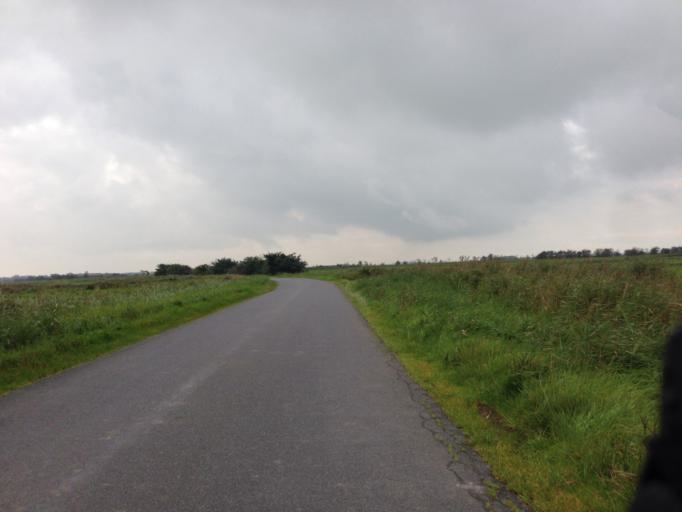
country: DE
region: Schleswig-Holstein
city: Oevenum
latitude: 54.7272
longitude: 8.5468
